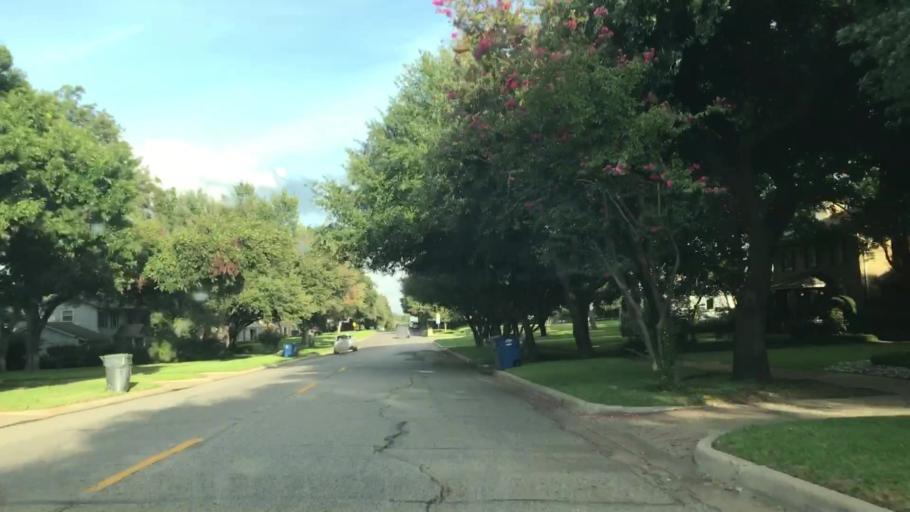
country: US
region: Texas
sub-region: Dallas County
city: Cockrell Hill
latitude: 32.7602
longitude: -96.8559
